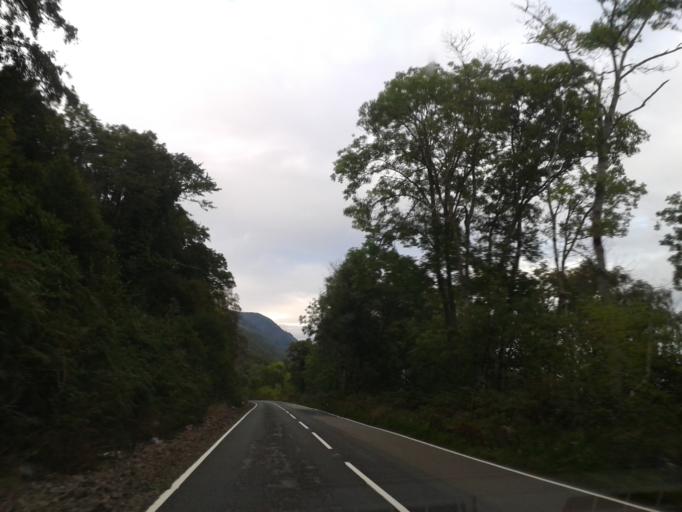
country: GB
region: Scotland
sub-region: Highland
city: Beauly
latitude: 57.3732
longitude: -4.3846
